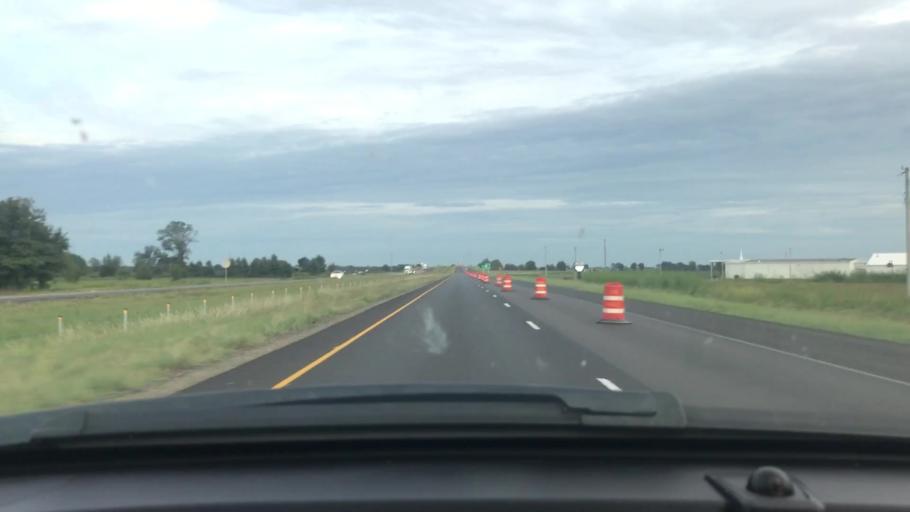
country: US
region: Arkansas
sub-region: Poinsett County
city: Trumann
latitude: 35.6373
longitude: -90.5068
